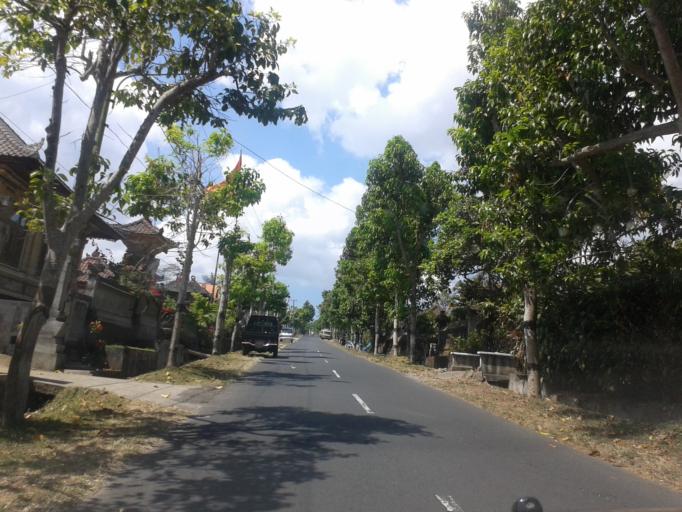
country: ID
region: Bali
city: Banjar Kedisan
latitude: -8.3100
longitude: 115.3341
